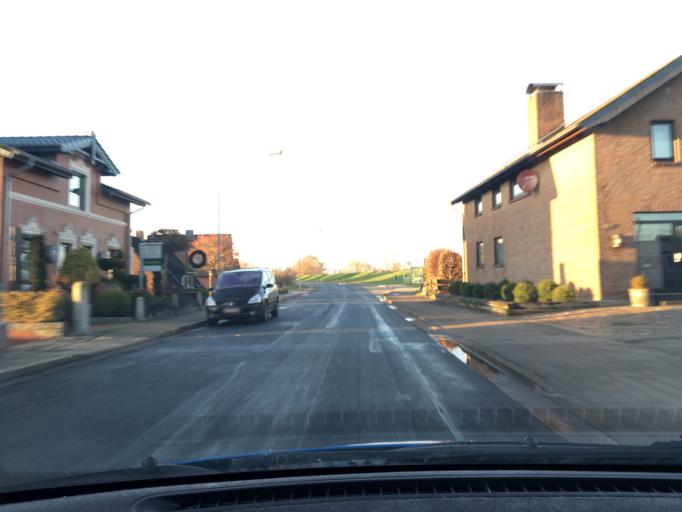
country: DE
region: Lower Saxony
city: Stelle
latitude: 53.4536
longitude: 10.0675
